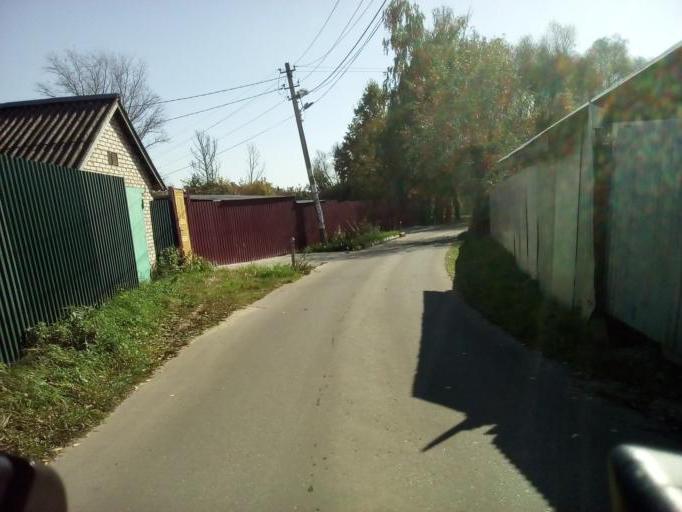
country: RU
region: Moskovskaya
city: Ramenskoye
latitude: 55.5468
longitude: 38.2882
